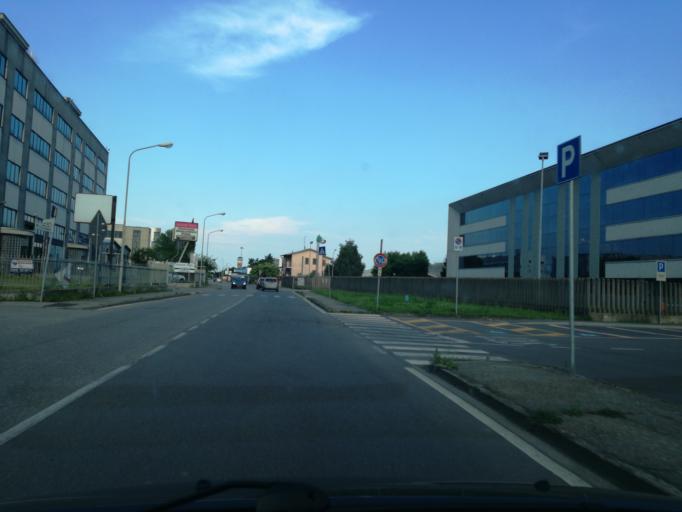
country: IT
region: Lombardy
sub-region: Provincia di Monza e Brianza
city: Cornate d'Adda
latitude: 45.6241
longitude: 9.4686
